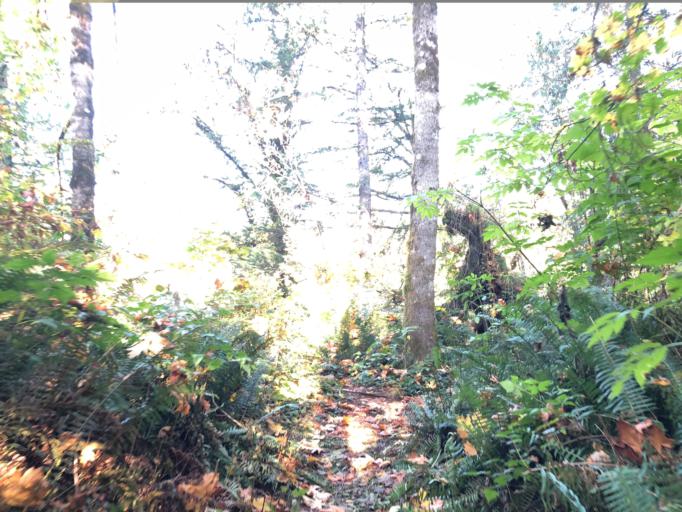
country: US
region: Washington
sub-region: King County
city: Ravensdale
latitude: 47.3212
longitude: -121.9043
